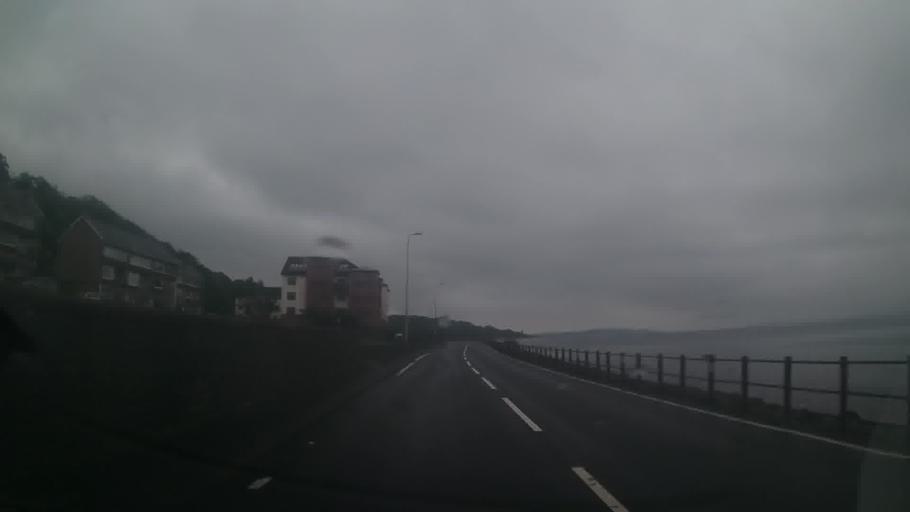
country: GB
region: Scotland
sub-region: North Ayrshire
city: Skelmorlie
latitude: 55.8571
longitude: -4.8899
